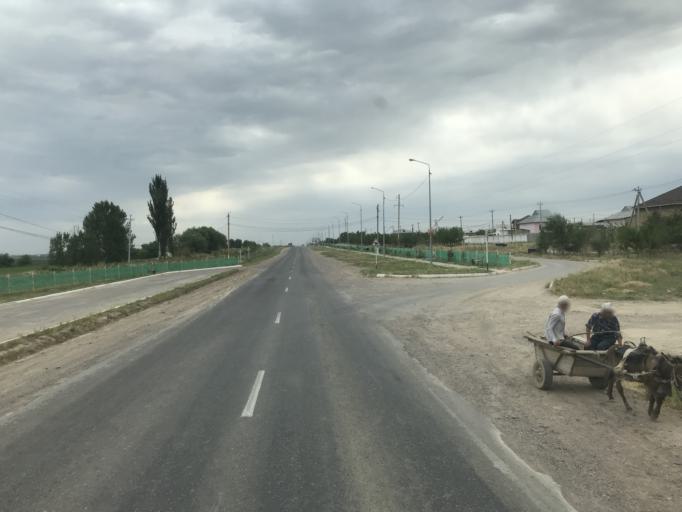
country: KZ
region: Ongtustik Qazaqstan
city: Saryaghash
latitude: 41.4206
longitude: 69.0890
